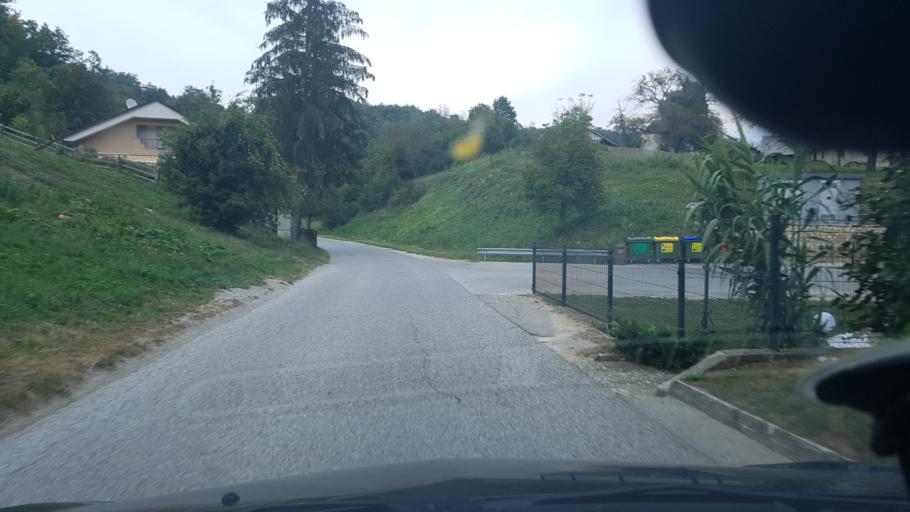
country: SI
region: Krsko
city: Senovo
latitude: 46.0189
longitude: 15.5034
